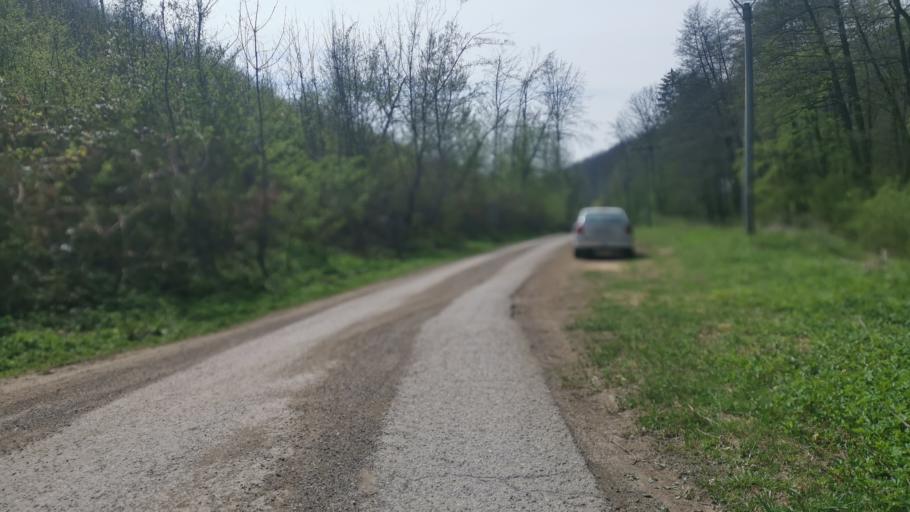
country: SK
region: Trnavsky
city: Smolenice
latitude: 48.5696
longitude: 17.4693
